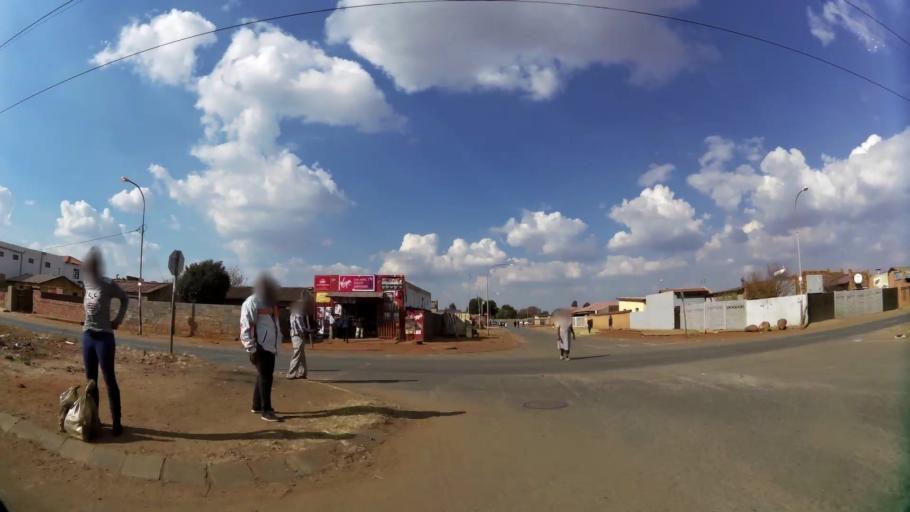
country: ZA
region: Gauteng
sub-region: City of Johannesburg Metropolitan Municipality
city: Soweto
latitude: -26.2231
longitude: 27.8581
